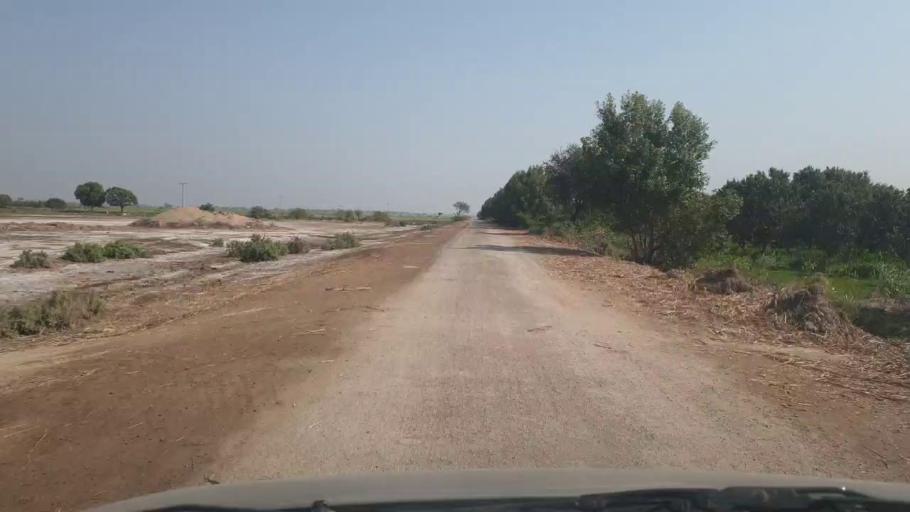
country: PK
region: Sindh
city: Digri
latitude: 25.2355
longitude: 69.1532
